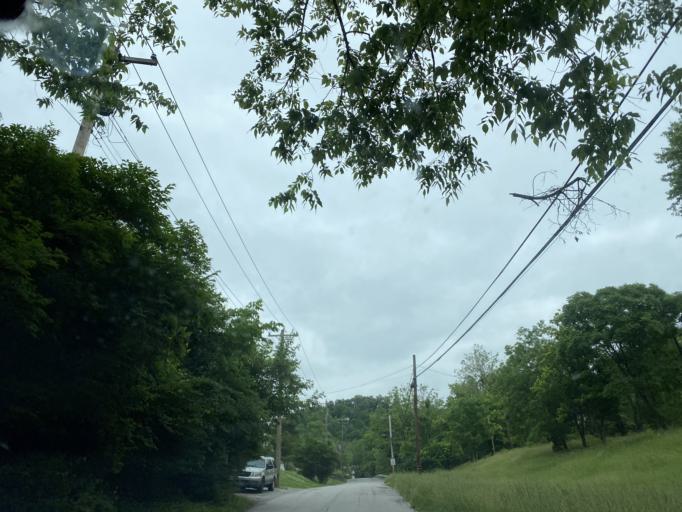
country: US
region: Kentucky
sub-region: Campbell County
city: Bellevue
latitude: 39.0996
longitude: -84.4674
